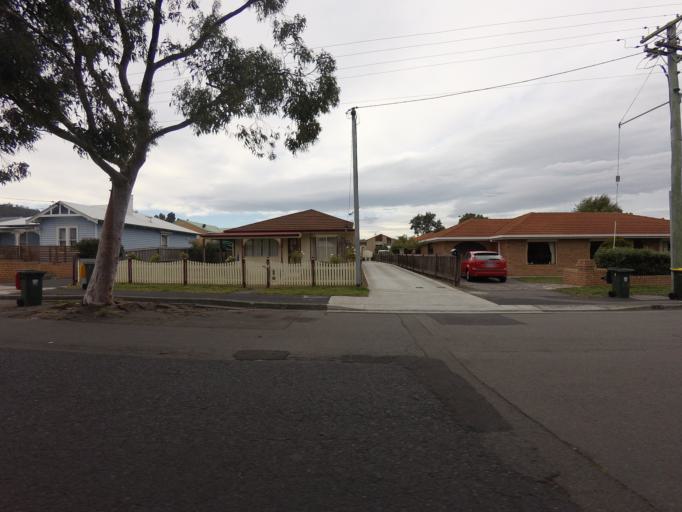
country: AU
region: Tasmania
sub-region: Clarence
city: Bellerive
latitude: -42.8777
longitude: 147.3788
